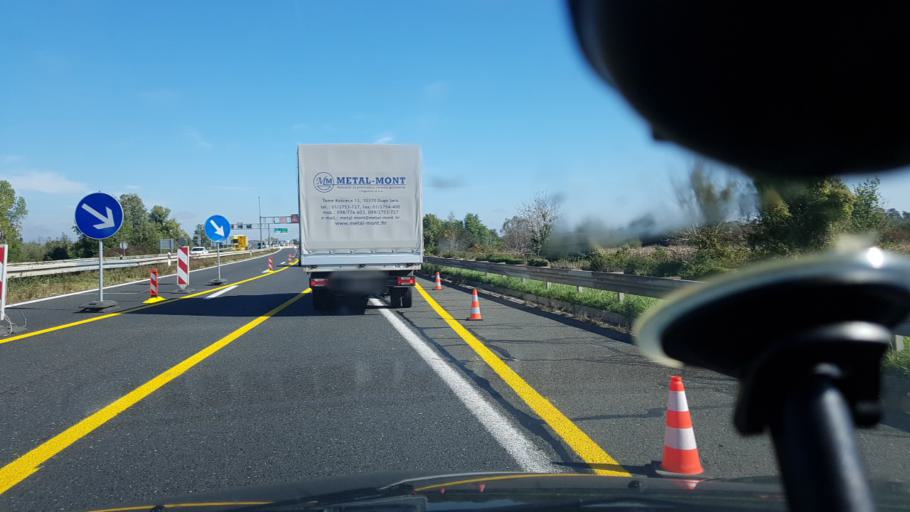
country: HR
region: Grad Zagreb
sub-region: Sesvete
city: Sesvete
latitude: 45.7796
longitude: 16.1141
